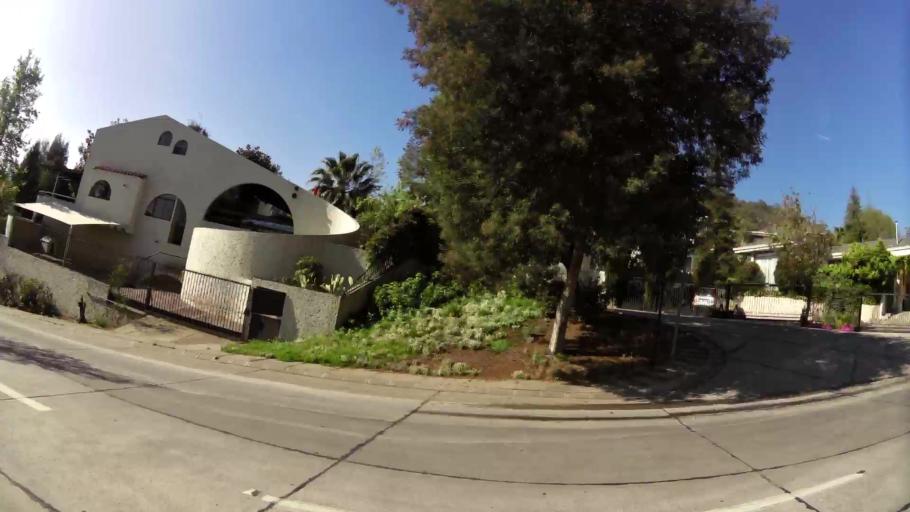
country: CL
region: Santiago Metropolitan
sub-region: Provincia de Santiago
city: Villa Presidente Frei, Nunoa, Santiago, Chile
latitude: -33.3723
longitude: -70.4966
